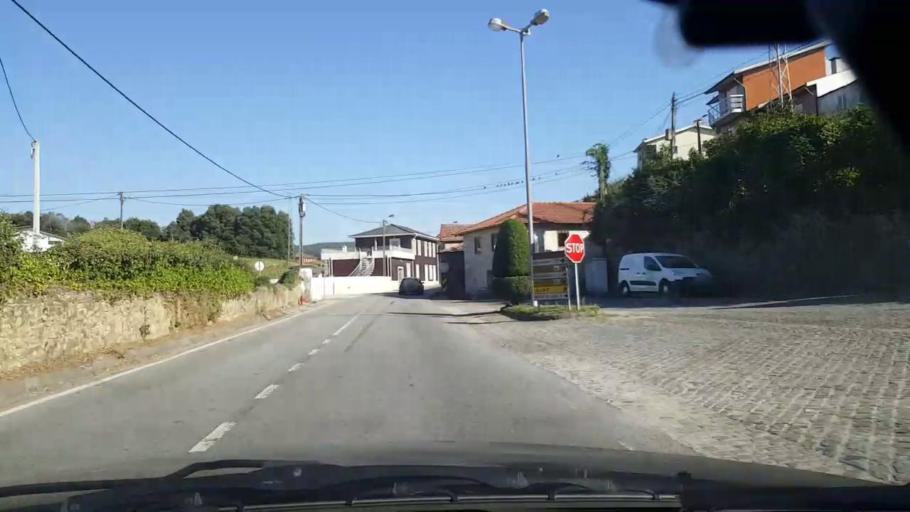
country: PT
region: Porto
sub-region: Vila do Conde
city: Arvore
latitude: 41.3335
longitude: -8.6661
